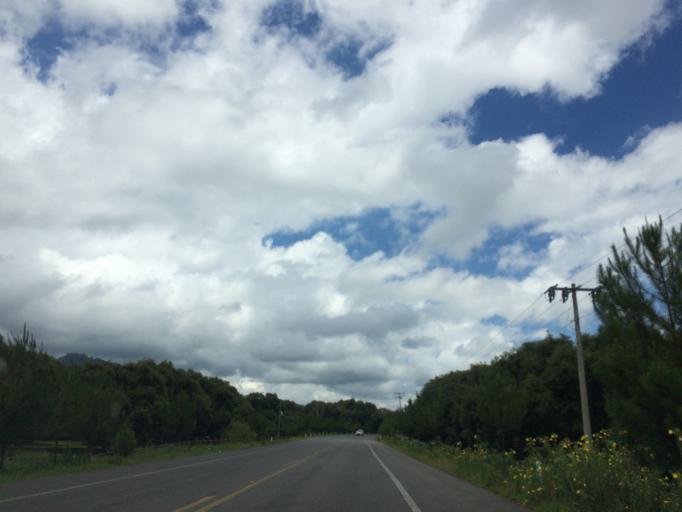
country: MX
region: Michoacan
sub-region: Uruapan
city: Santa Ana Zirosto
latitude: 19.5433
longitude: -102.3235
